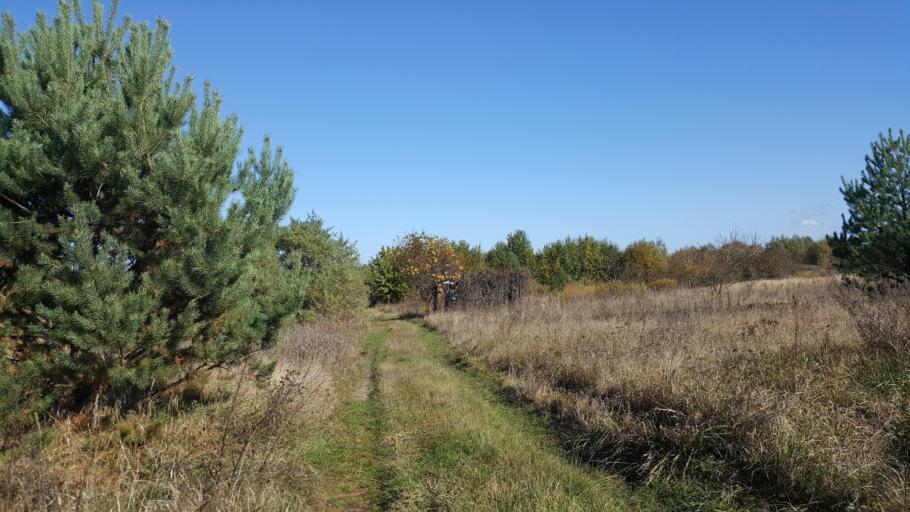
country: BY
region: Brest
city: Kamyanyets
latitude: 52.4334
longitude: 23.8837
